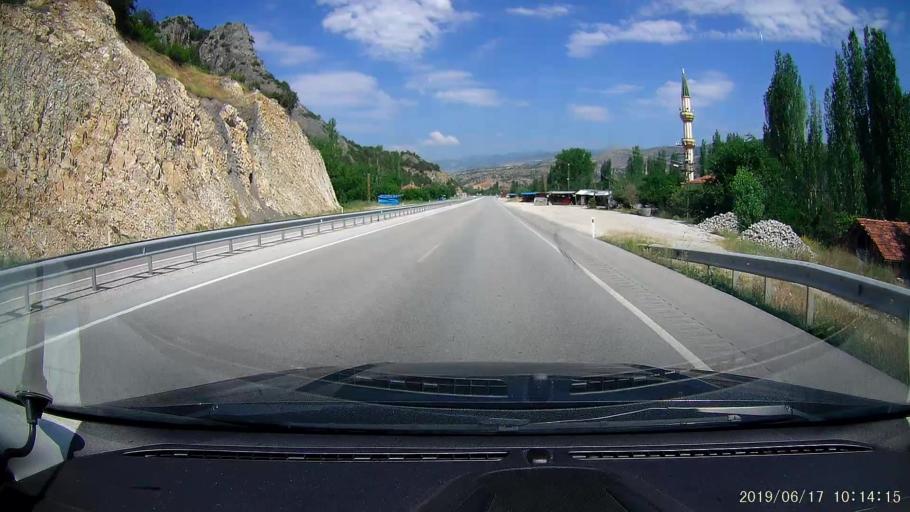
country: TR
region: Amasya
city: Saraycik
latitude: 40.9887
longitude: 35.0299
